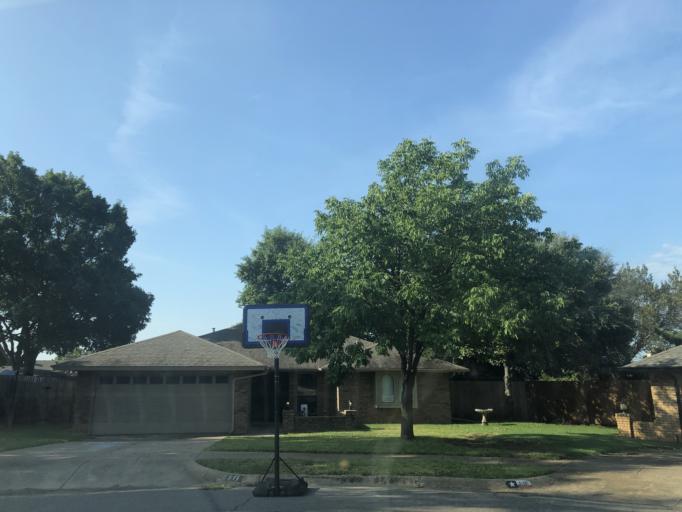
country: US
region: Texas
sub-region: Tarrant County
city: Euless
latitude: 32.8724
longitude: -97.0912
